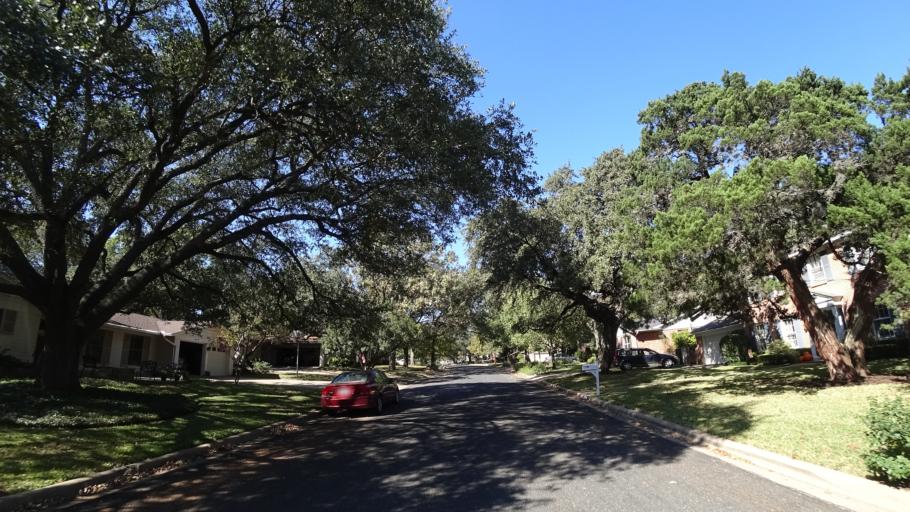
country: US
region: Texas
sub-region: Williamson County
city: Jollyville
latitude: 30.3795
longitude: -97.7481
